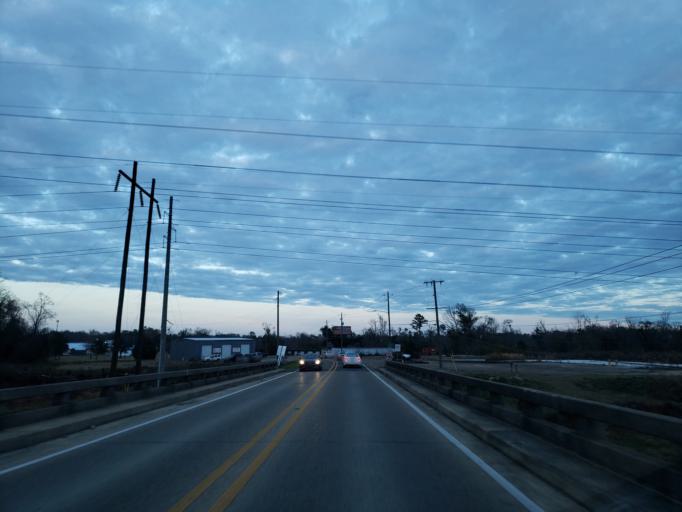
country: US
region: Mississippi
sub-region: Forrest County
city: Petal
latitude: 31.3272
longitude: -89.2659
